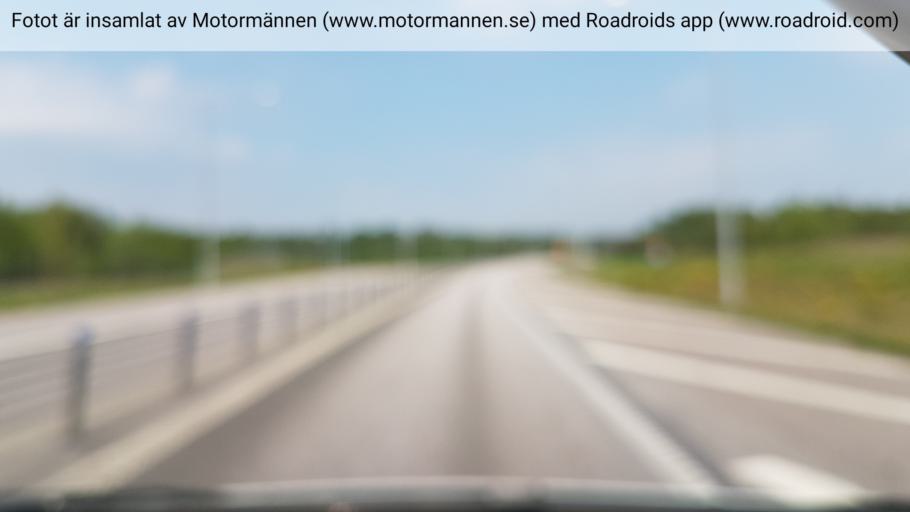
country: SE
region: Vaestra Goetaland
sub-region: Skovde Kommun
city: Skultorp
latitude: 58.3649
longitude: 13.8581
